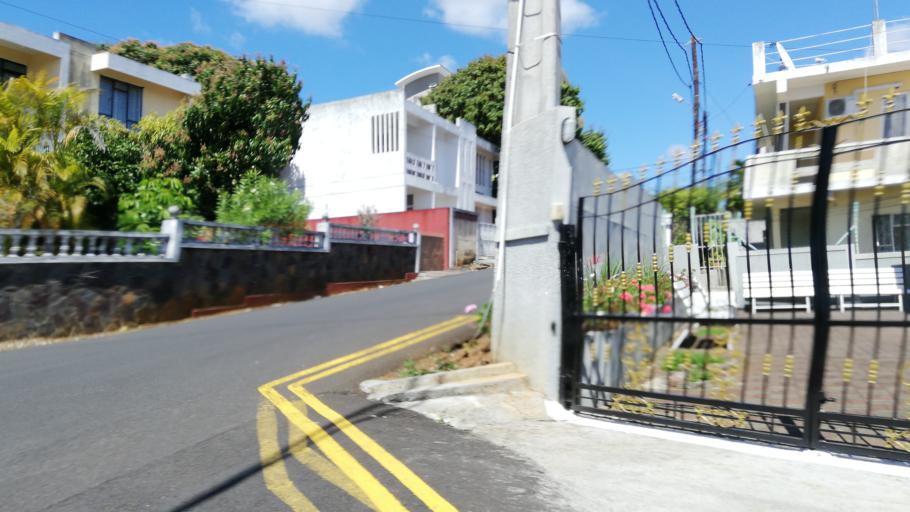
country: MU
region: Plaines Wilhems
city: Ebene
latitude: -20.2285
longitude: 57.4718
